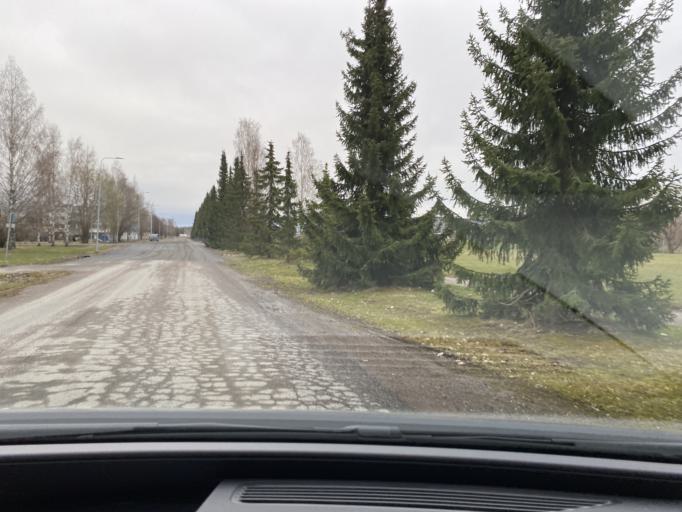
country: FI
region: Satakunta
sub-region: Pori
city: Huittinen
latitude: 61.1860
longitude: 22.6907
